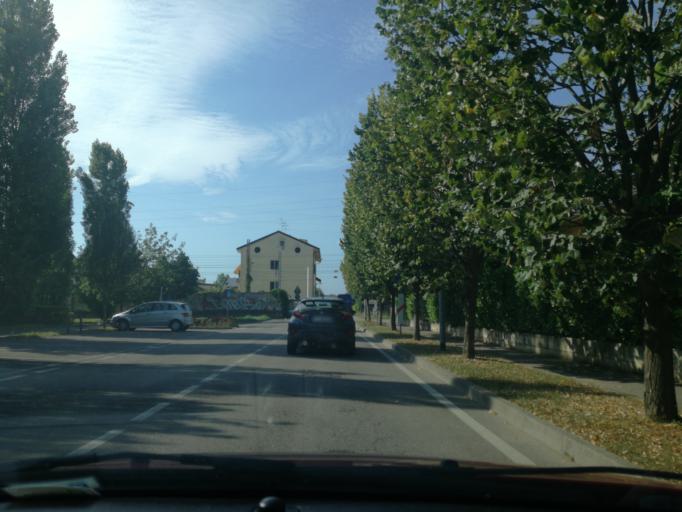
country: IT
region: Lombardy
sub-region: Provincia di Monza e Brianza
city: Velasca
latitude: 45.6330
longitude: 9.3406
